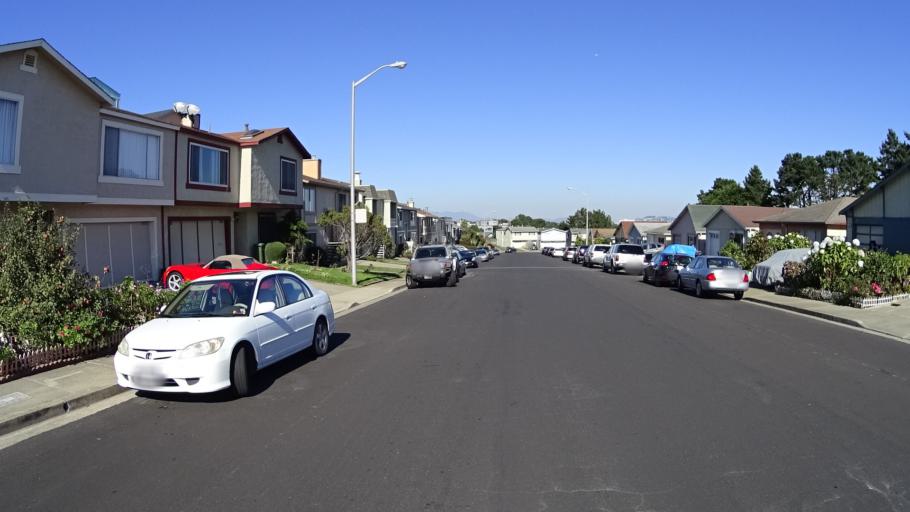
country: US
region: California
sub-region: San Mateo County
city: Colma
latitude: 37.6620
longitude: -122.4746
